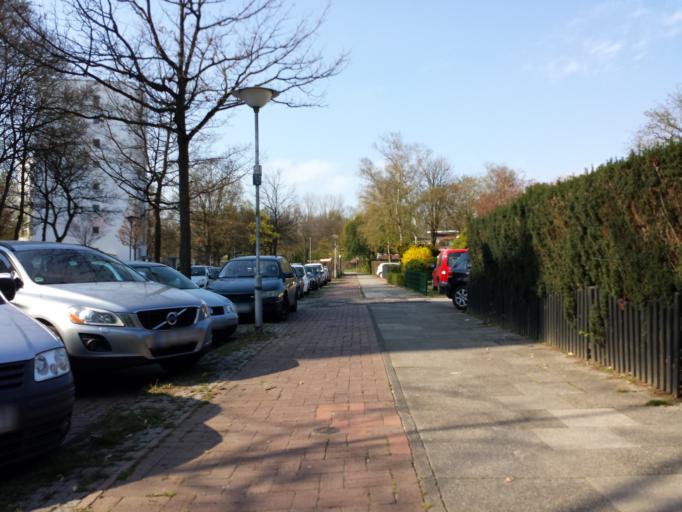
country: DE
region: Lower Saxony
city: Lilienthal
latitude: 53.0849
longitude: 8.8988
